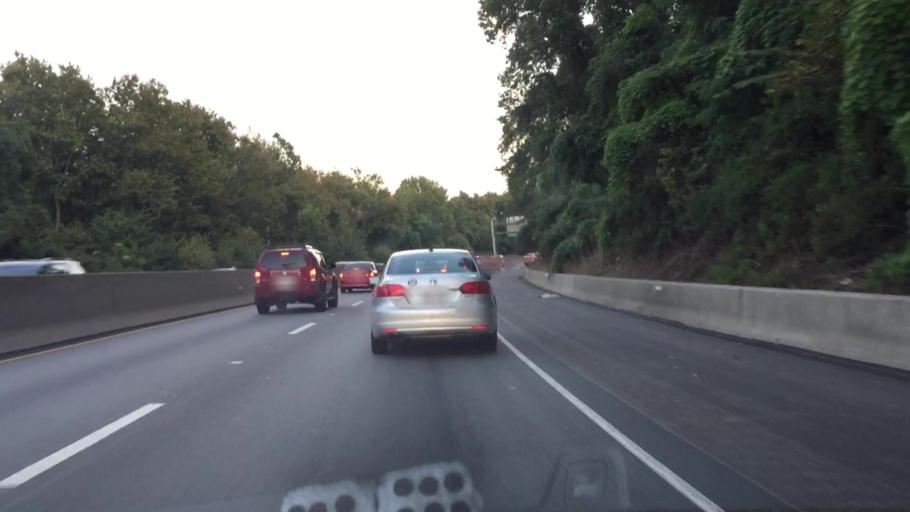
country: US
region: Pennsylvania
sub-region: Montgomery County
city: Conshohocken
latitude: 40.0707
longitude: -75.2815
